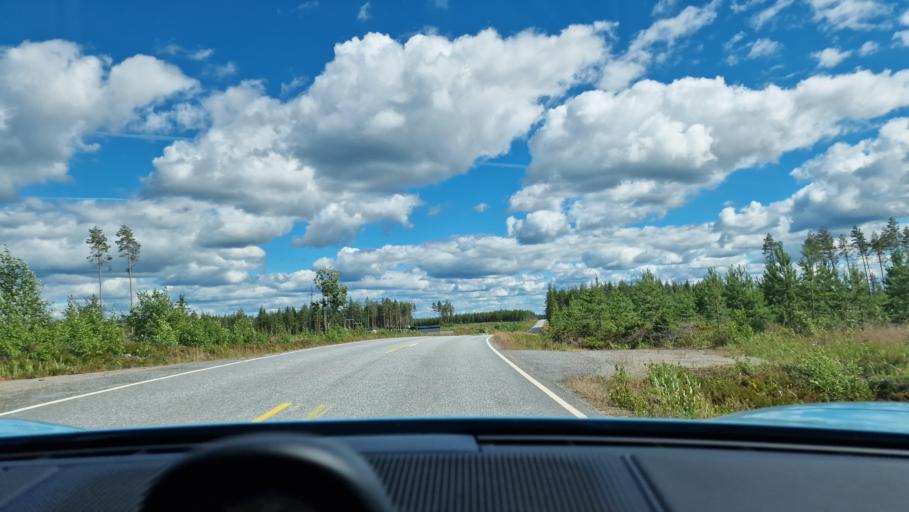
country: FI
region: Central Finland
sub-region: Saarijaervi-Viitasaari
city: Pylkoenmaeki
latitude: 62.6646
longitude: 24.5467
